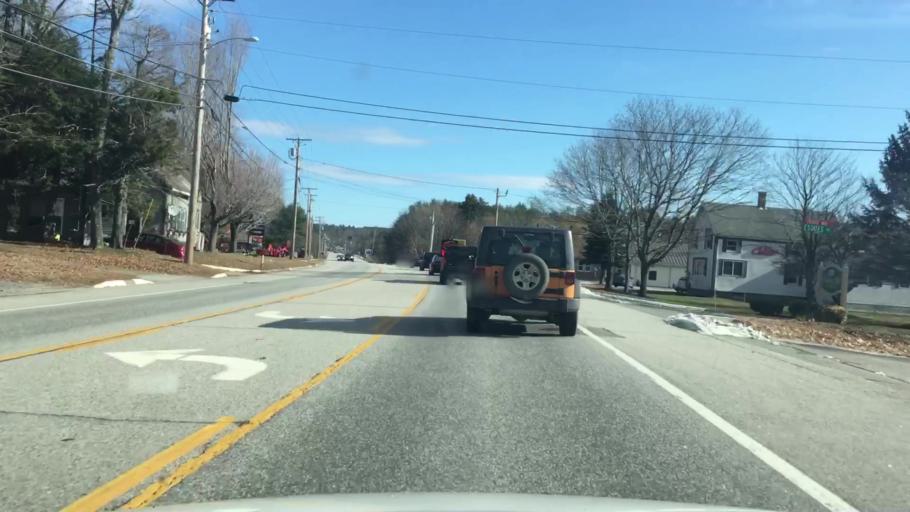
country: US
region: Maine
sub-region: Kennebec County
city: Manchester
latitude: 44.3234
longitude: -69.8728
